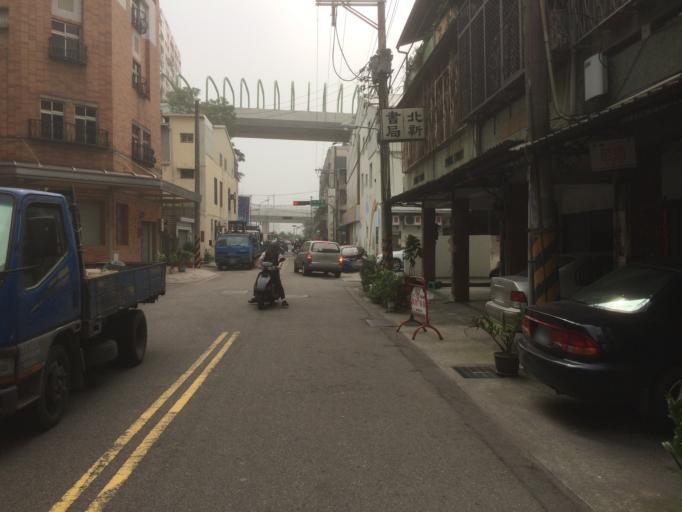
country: TW
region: Taiwan
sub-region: Taichung City
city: Taichung
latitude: 24.1788
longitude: 120.6997
